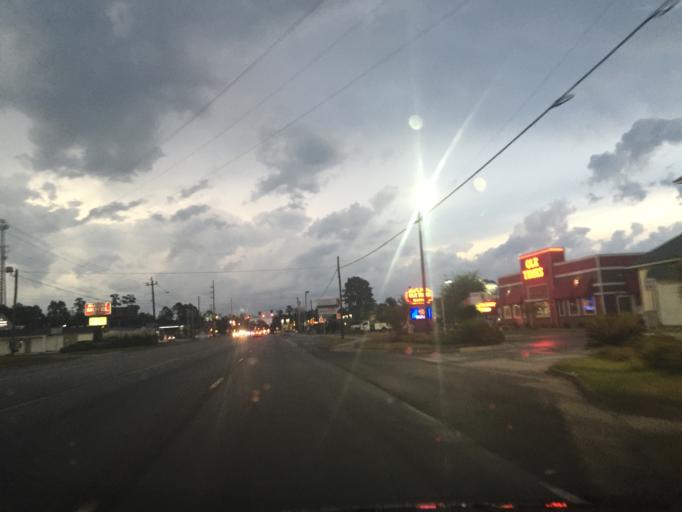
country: US
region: Georgia
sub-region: Liberty County
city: Hinesville
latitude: 31.8519
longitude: -81.5816
